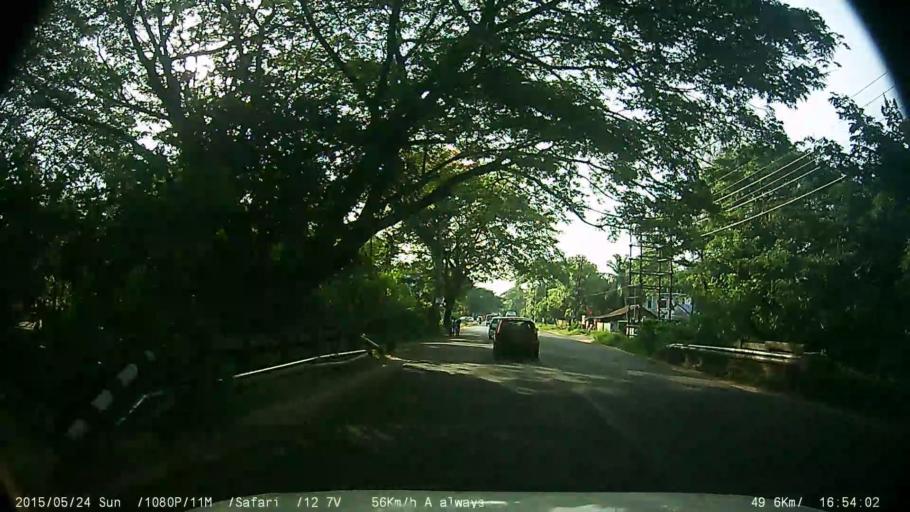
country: IN
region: Kerala
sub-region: Alappuzha
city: Shertallai
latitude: 9.6789
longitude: 76.3370
